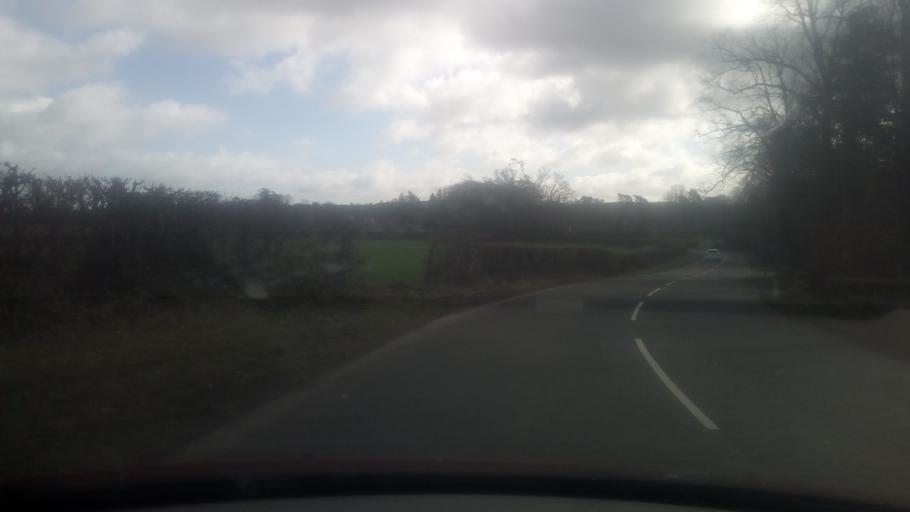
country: GB
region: Scotland
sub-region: The Scottish Borders
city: Saint Boswells
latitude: 55.5670
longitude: -2.6360
